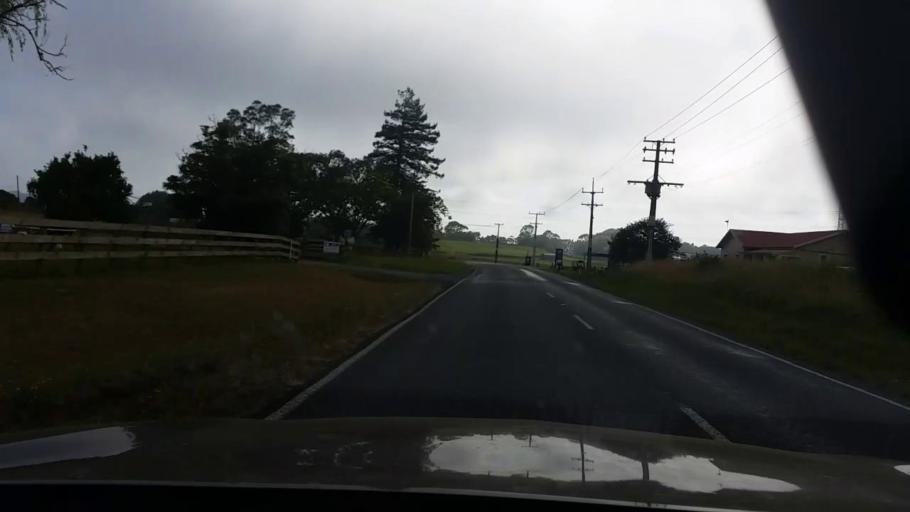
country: NZ
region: Waikato
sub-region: Hamilton City
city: Hamilton
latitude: -37.6198
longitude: 175.3363
